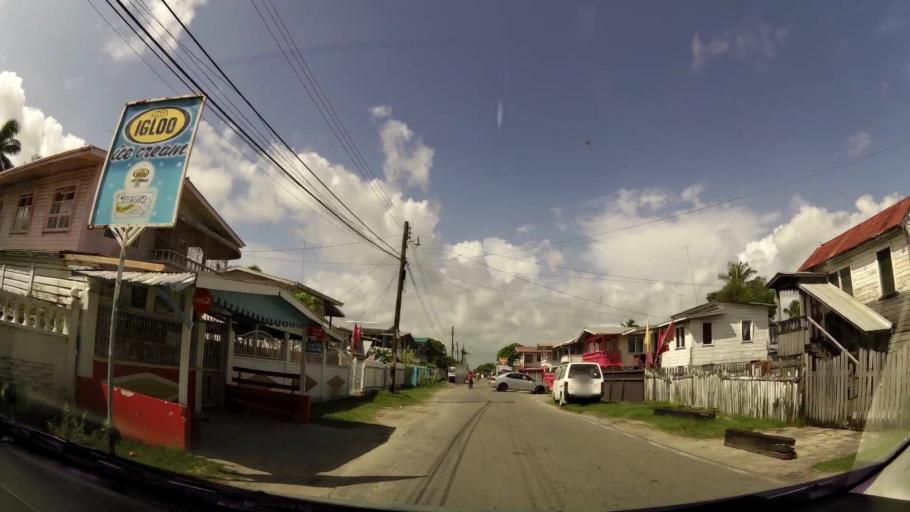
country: GY
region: Demerara-Mahaica
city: Mahaica Village
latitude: 6.7585
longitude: -57.9919
